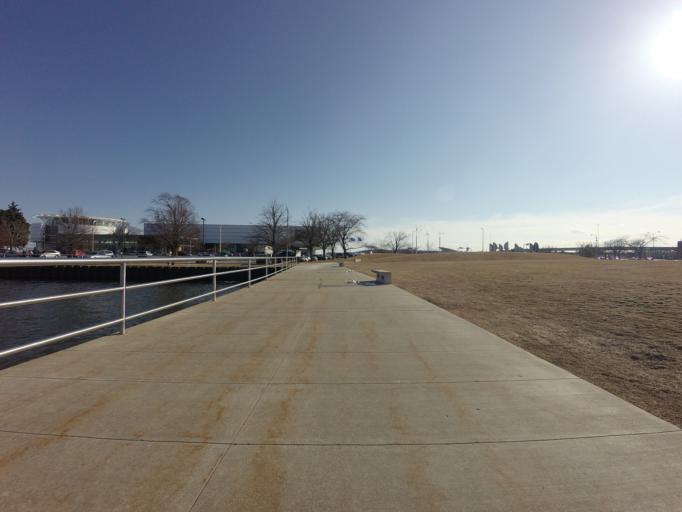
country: US
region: Wisconsin
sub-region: Milwaukee County
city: Milwaukee
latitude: 43.0381
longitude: -87.8967
